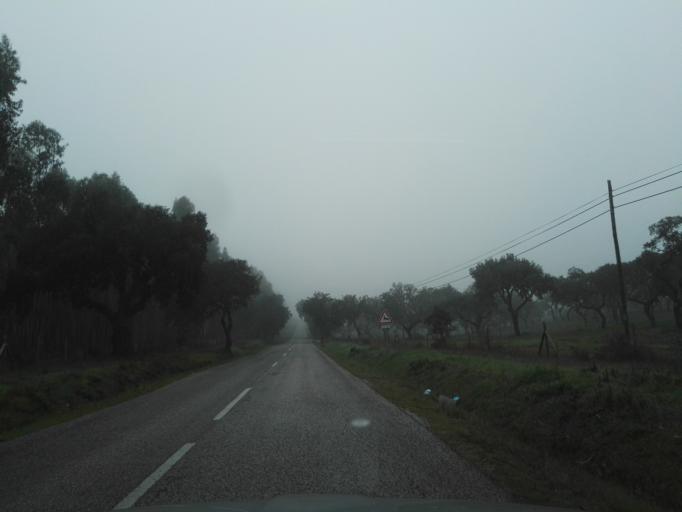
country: PT
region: Evora
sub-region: Montemor-O-Novo
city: Montemor-o-Novo
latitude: 38.7792
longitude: -8.2139
